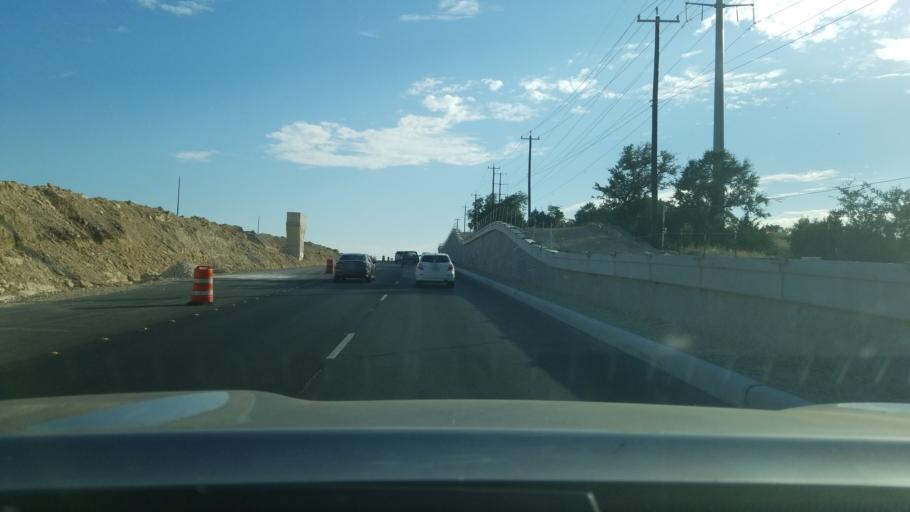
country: US
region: Texas
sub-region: Comal County
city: Bulverde
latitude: 29.7144
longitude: -98.4474
